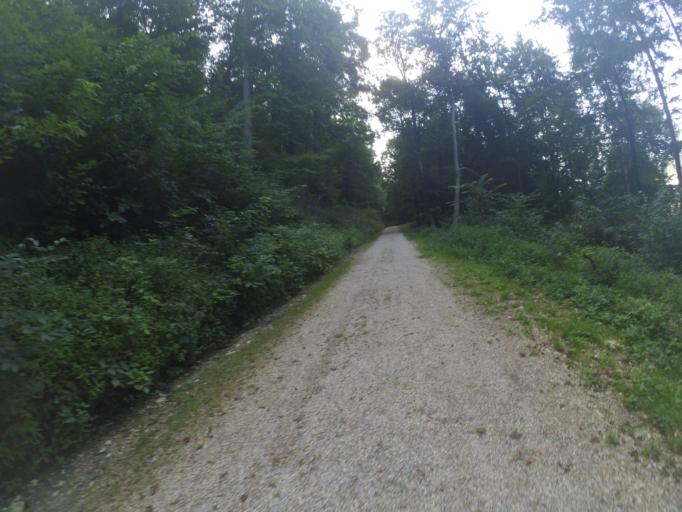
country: DE
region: Baden-Wuerttemberg
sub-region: Tuebingen Region
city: Bad Urach
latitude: 48.4945
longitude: 9.3838
